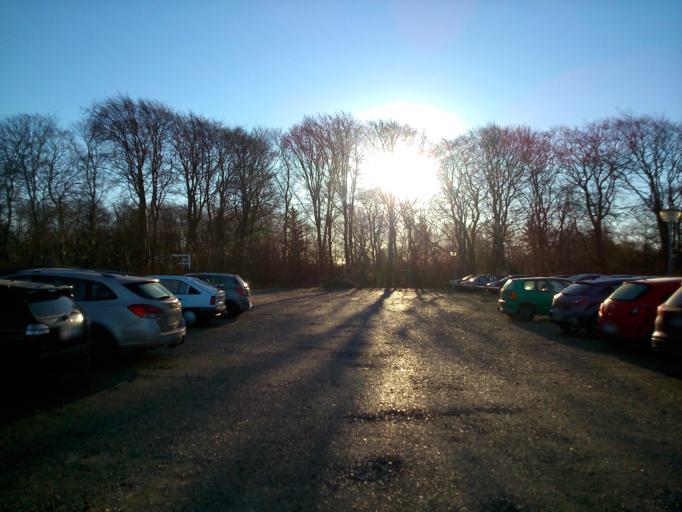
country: DK
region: Central Jutland
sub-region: Holstebro Kommune
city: Holstebro
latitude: 56.3624
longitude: 8.6285
